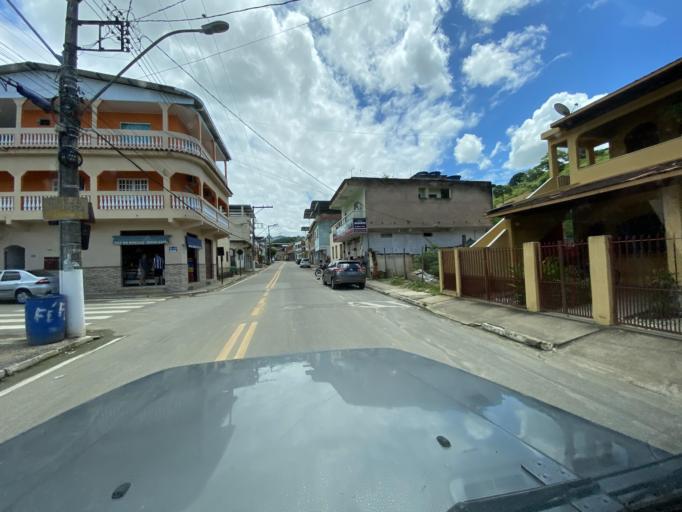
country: BR
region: Espirito Santo
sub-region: Jeronimo Monteiro
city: Jeronimo Monteiro
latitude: -20.7920
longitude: -41.3992
